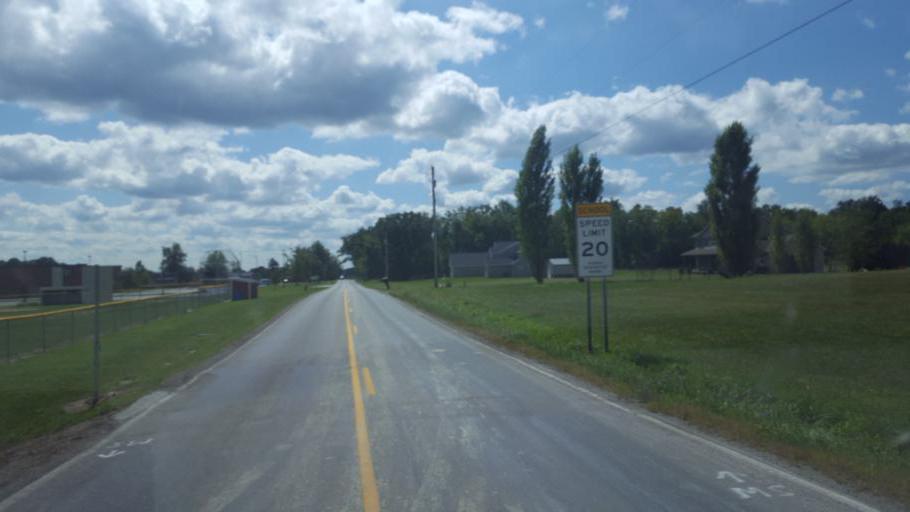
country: US
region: Ohio
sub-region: Ashland County
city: Ashland
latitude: 40.9703
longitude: -82.2820
